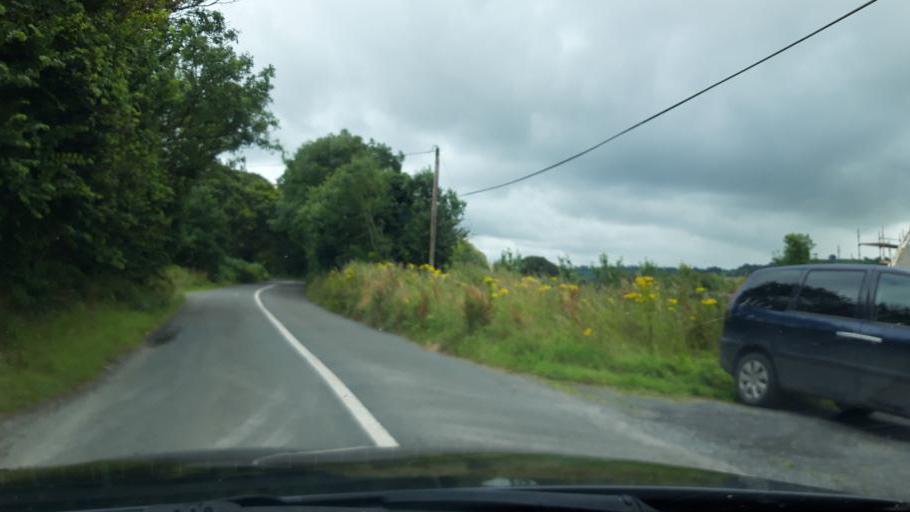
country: IE
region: Munster
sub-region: County Cork
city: Castlemartyr
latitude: 52.1313
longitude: -7.9923
